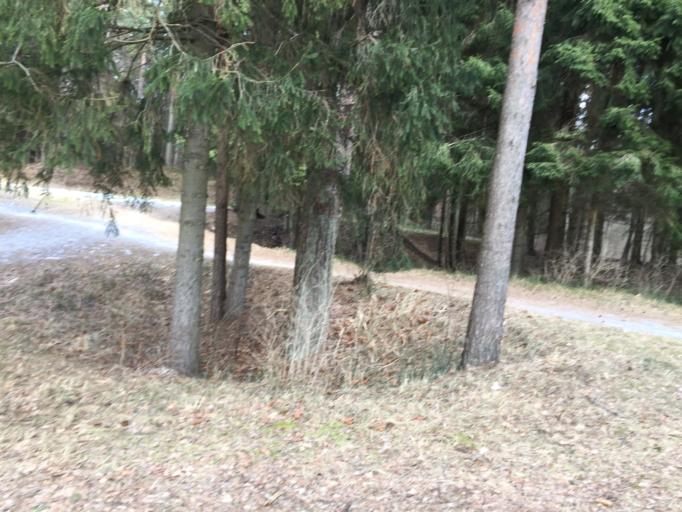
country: LV
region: Valmieras Rajons
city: Valmiera
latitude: 57.5355
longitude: 25.4369
